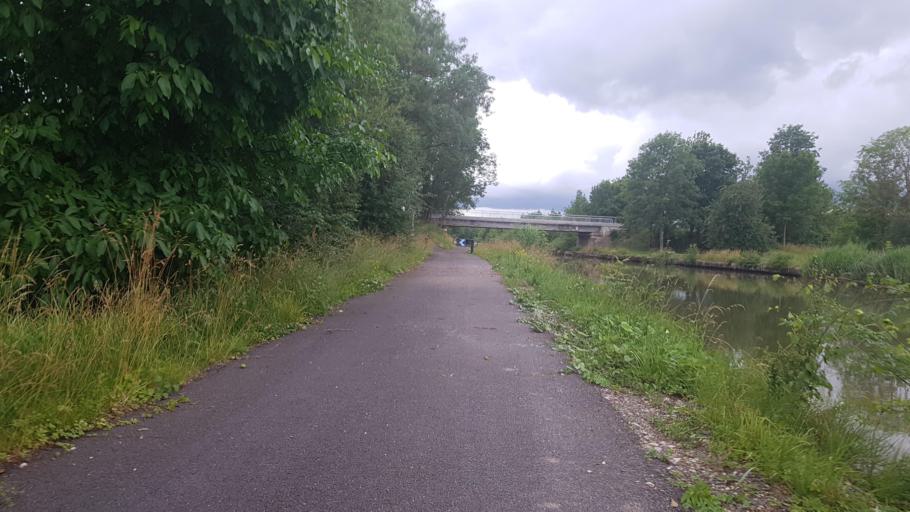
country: FR
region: Lorraine
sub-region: Departement de Meurthe-et-Moselle
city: Chanteheux
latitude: 48.6797
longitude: 6.6077
